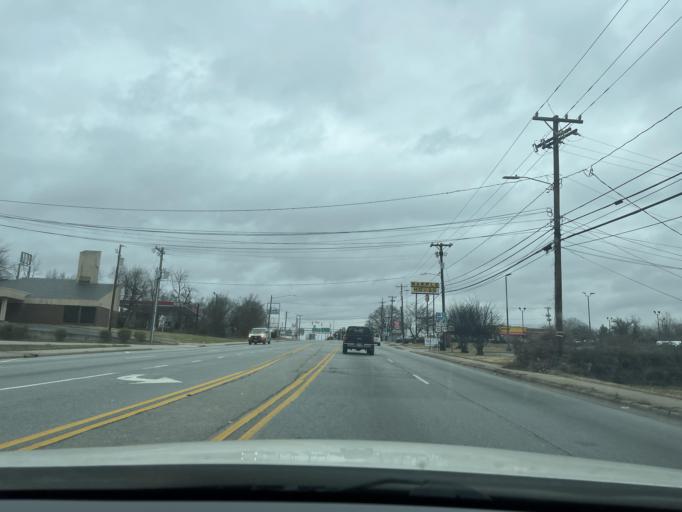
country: US
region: North Carolina
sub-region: Guilford County
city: Greensboro
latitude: 36.0308
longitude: -79.8013
